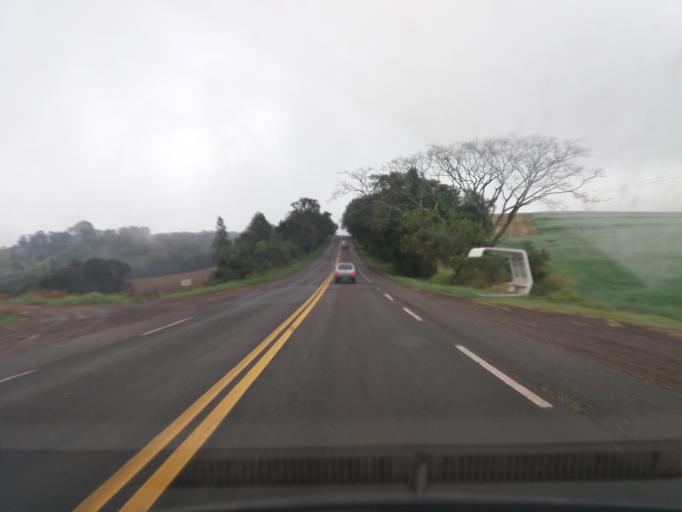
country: BR
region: Parana
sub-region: Realeza
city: Realeza
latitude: -25.8381
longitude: -53.5167
